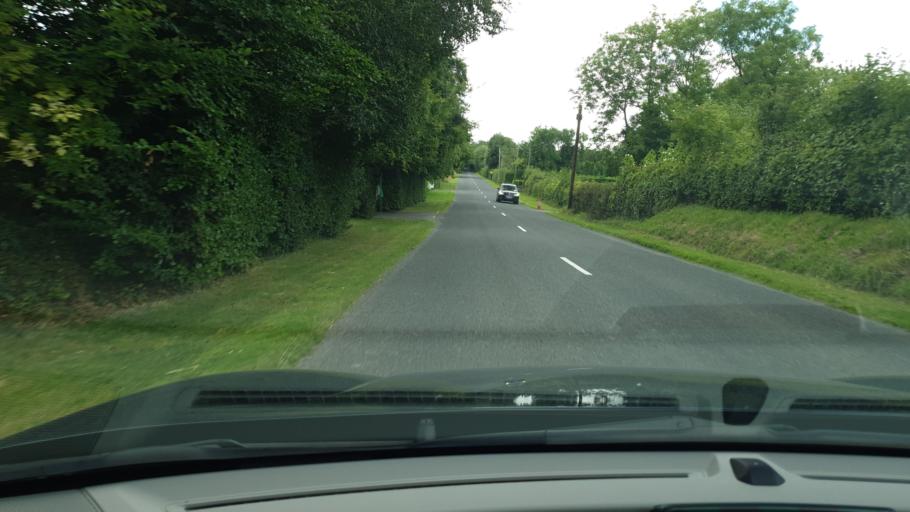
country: IE
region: Leinster
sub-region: An Mhi
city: Dunshaughlin
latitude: 53.5660
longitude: -6.5823
